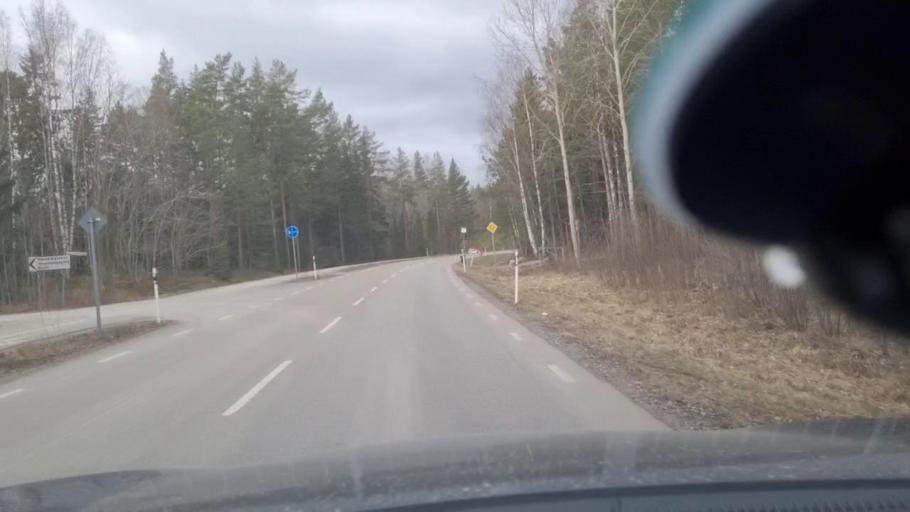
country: SE
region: Stockholm
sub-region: Jarfalla Kommun
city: Jakobsberg
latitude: 59.4233
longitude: 17.7756
